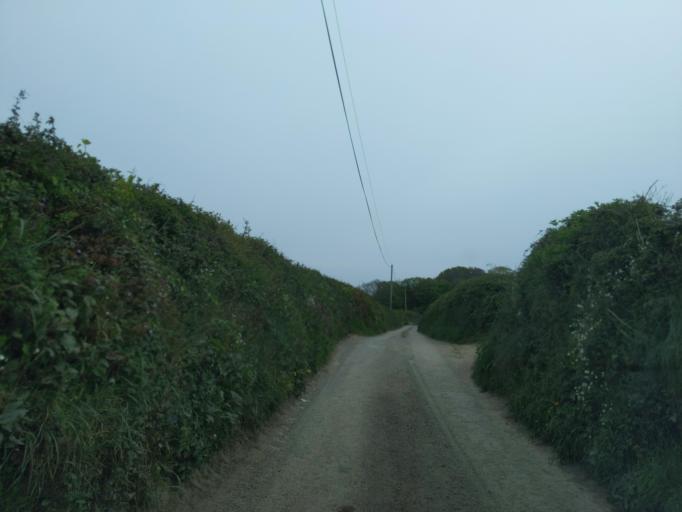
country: GB
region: England
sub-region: Cornwall
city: St Austell
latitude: 50.3096
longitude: -4.7660
